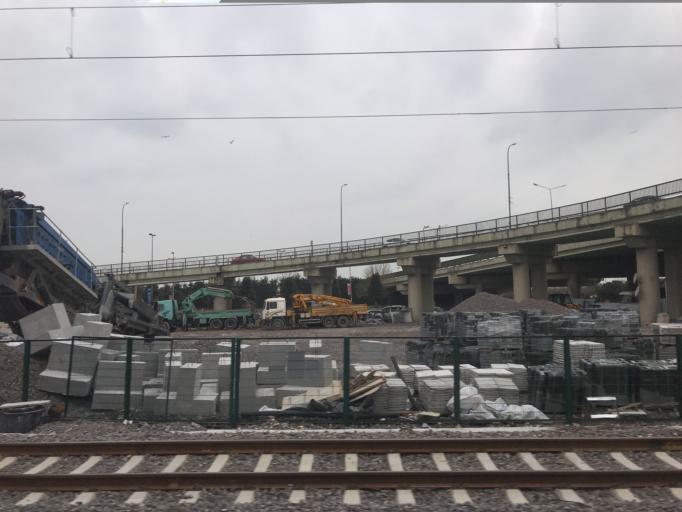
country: TR
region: Istanbul
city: Maltepe
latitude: 40.9330
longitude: 29.1181
